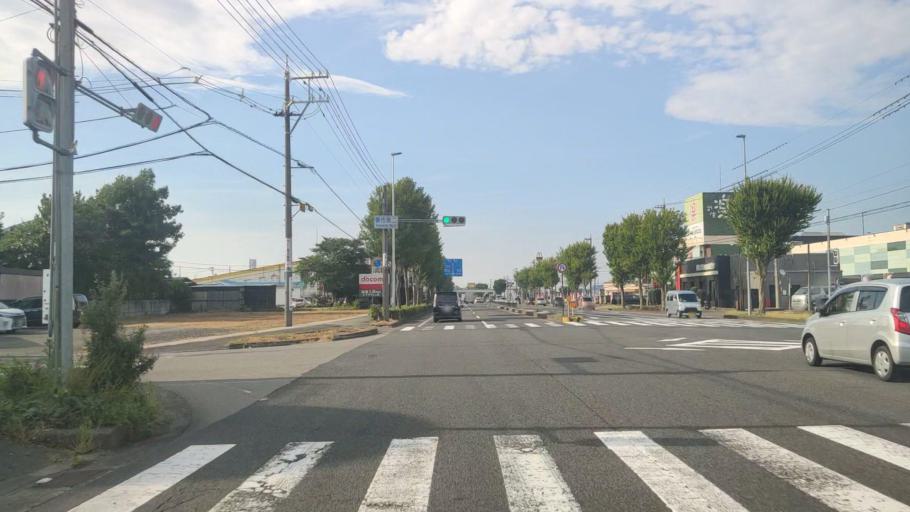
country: JP
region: Fukui
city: Takefu
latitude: 35.9059
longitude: 136.1921
